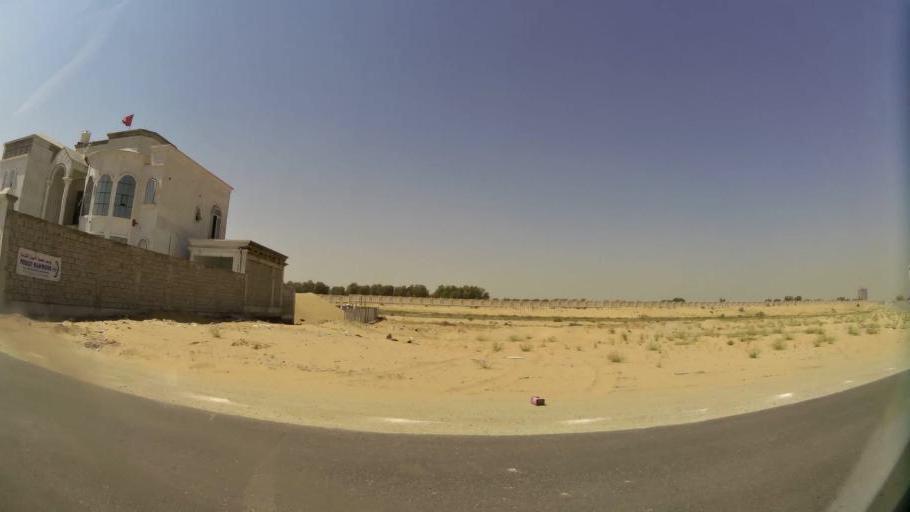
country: AE
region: Ajman
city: Ajman
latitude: 25.4046
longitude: 55.5331
